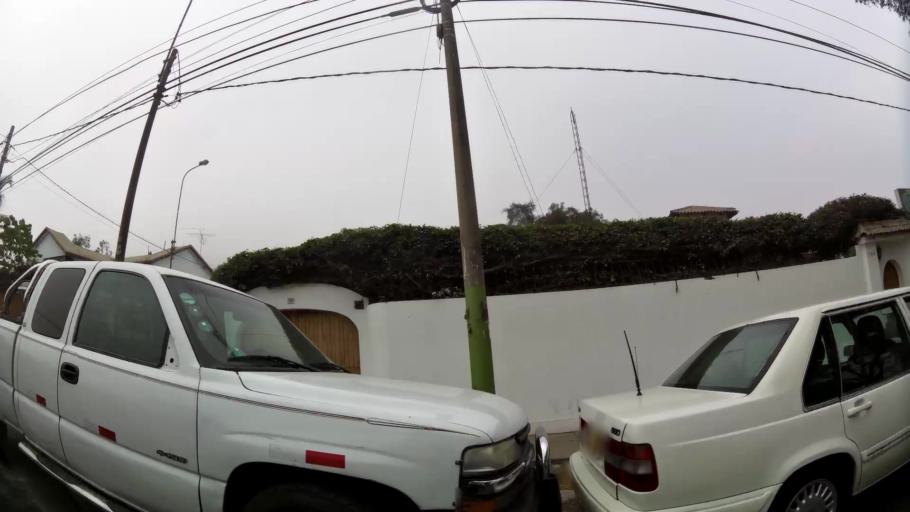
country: PE
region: Lima
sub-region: Lima
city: Chaclacayo
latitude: -11.9763
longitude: -76.7695
